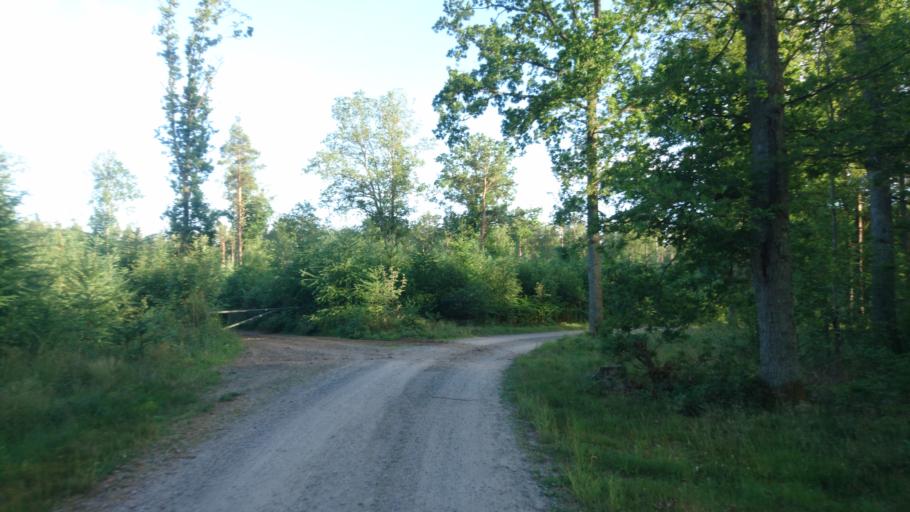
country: SE
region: Blekinge
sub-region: Karlshamns Kommun
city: Morrum
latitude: 56.1542
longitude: 14.7999
